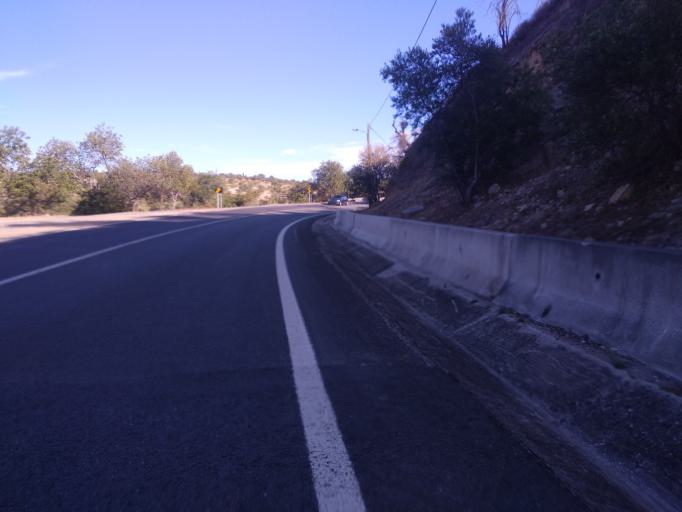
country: PT
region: Faro
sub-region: Sao Bras de Alportel
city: Sao Bras de Alportel
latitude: 37.1041
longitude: -7.9054
